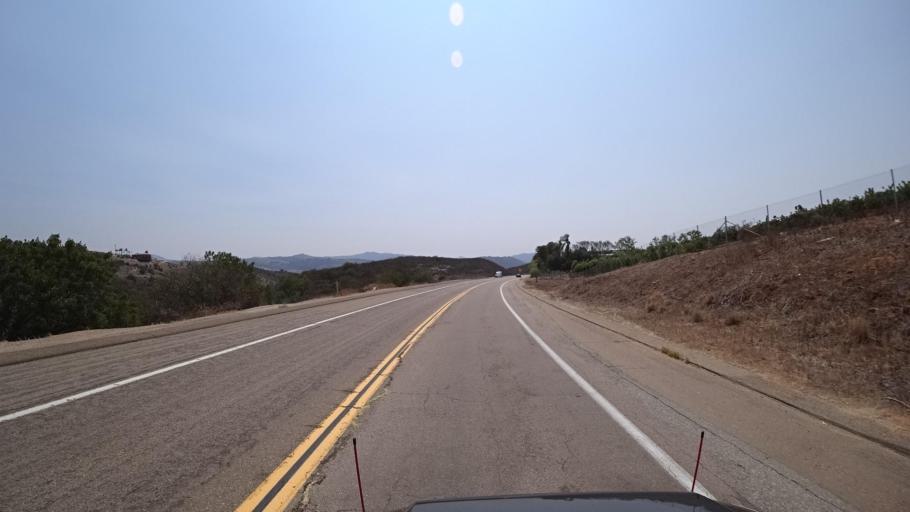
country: US
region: California
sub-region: San Diego County
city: Bonsall
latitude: 33.2939
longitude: -117.1514
